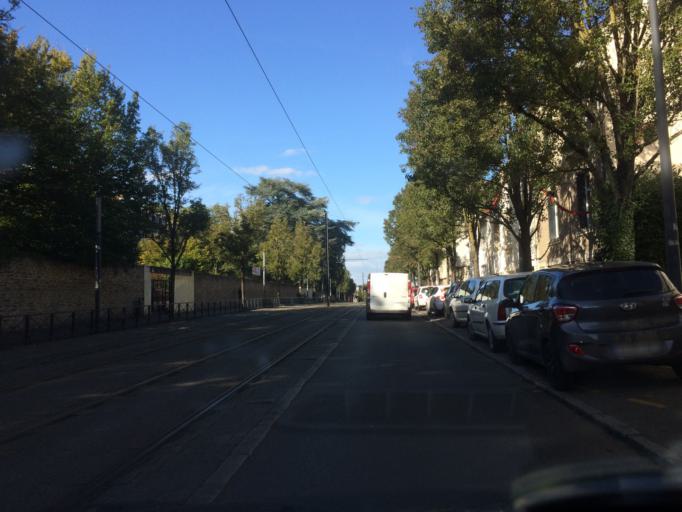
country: FR
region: Pays de la Loire
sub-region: Departement de la Loire-Atlantique
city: Nantes
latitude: 47.2358
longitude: -1.5565
